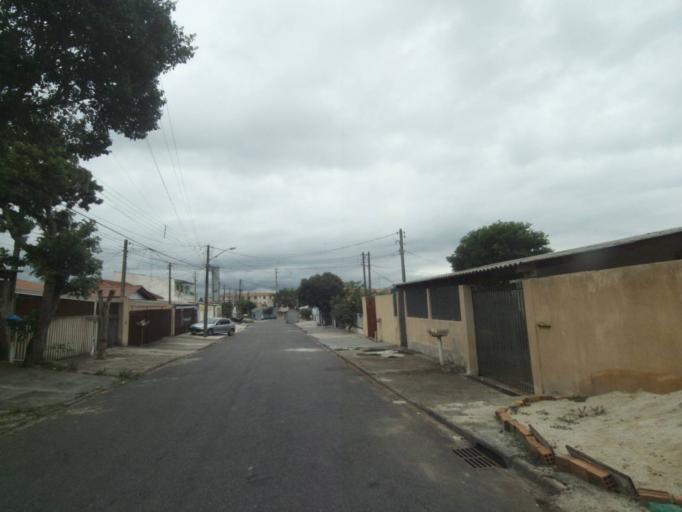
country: BR
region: Parana
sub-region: Sao Jose Dos Pinhais
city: Sao Jose dos Pinhais
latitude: -25.5471
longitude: -49.2653
